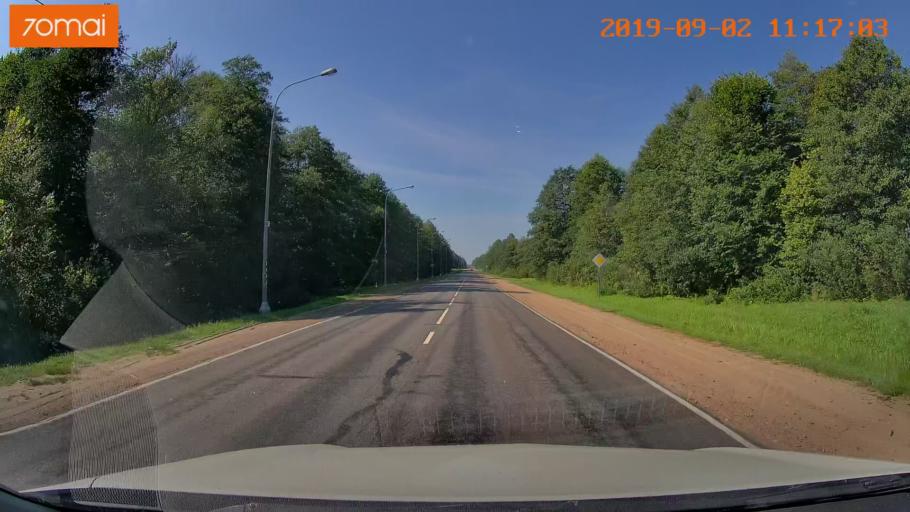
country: RU
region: Smolensk
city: Yekimovichi
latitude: 54.0641
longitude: 33.1265
